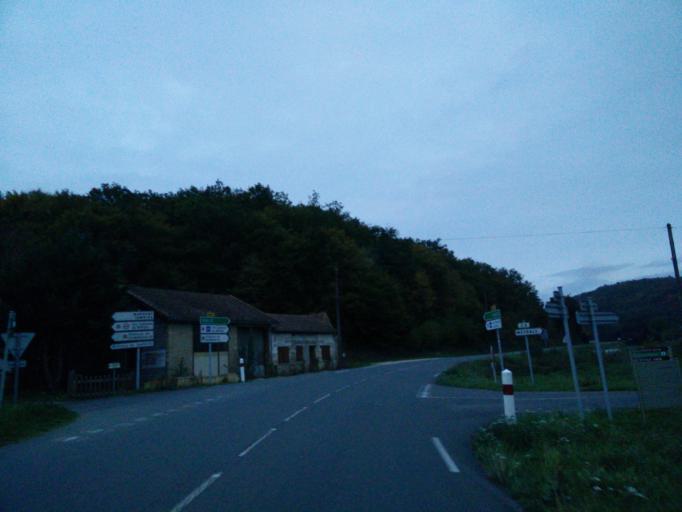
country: FR
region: Aquitaine
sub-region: Departement de la Dordogne
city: Saint-Cyprien
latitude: 44.9173
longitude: 1.1074
